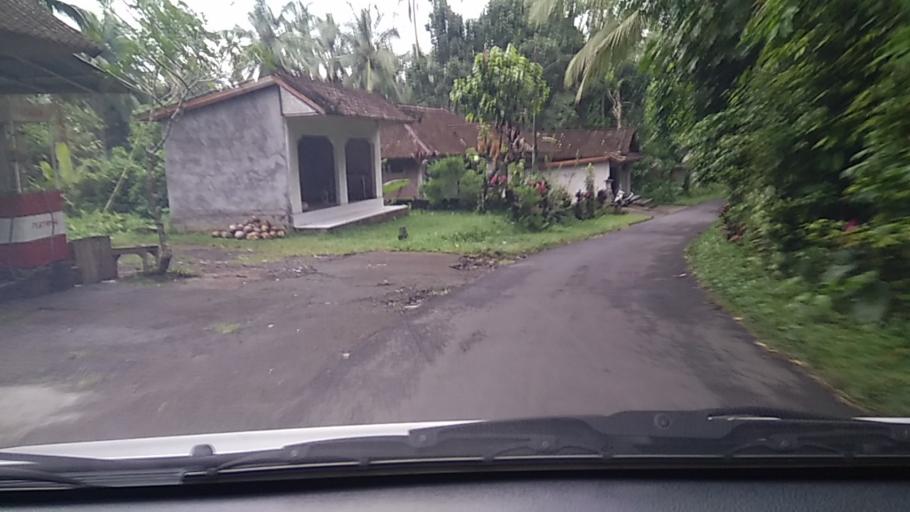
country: ID
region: Bali
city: Tegalalang
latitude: -8.4214
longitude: 115.2808
